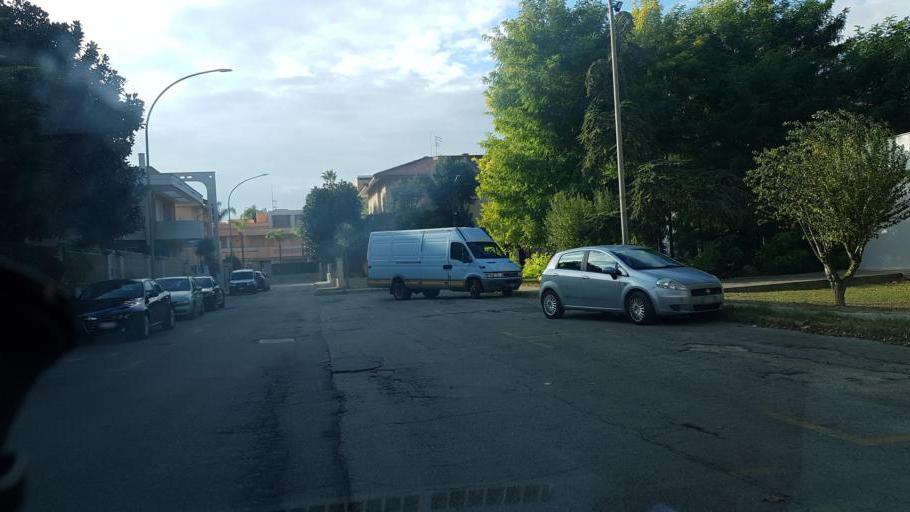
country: IT
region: Apulia
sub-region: Provincia di Brindisi
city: Francavilla Fontana
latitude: 40.5351
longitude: 17.5844
